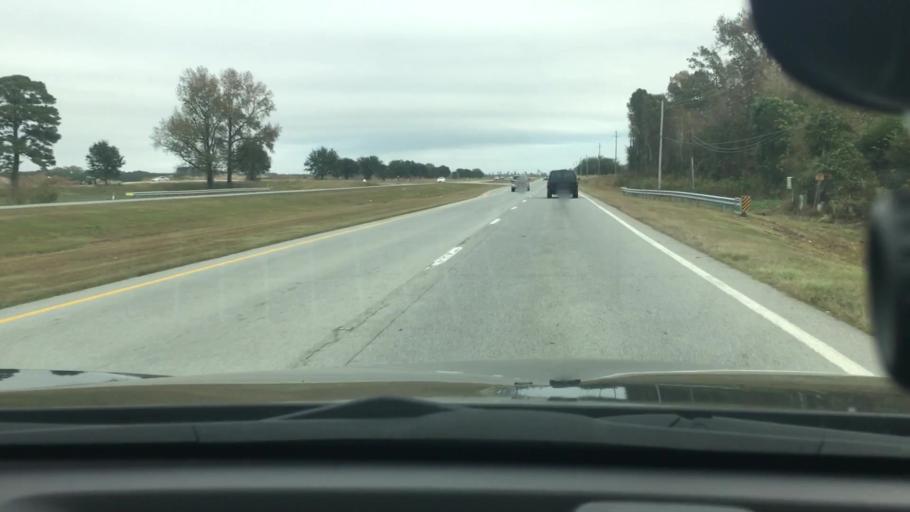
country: US
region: North Carolina
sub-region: Pitt County
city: Greenville
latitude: 35.6256
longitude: -77.2777
